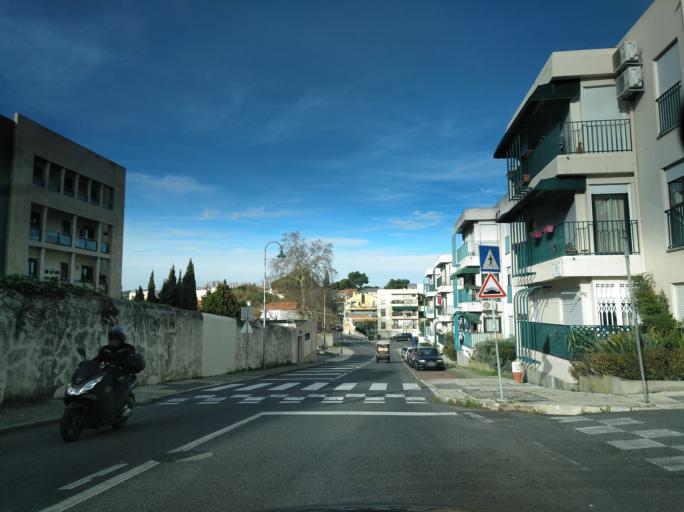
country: PT
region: Lisbon
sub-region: Oeiras
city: Alges
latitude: 38.7141
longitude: -9.2146
